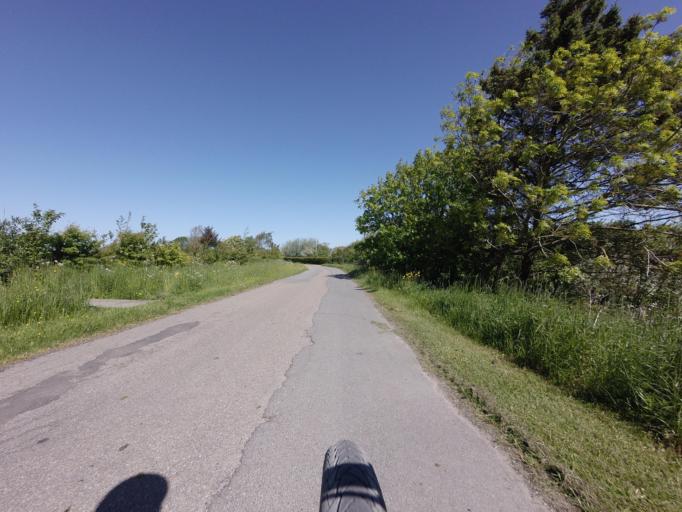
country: DK
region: North Denmark
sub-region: Hjorring Kommune
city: Hjorring
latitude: 57.4528
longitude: 9.8965
